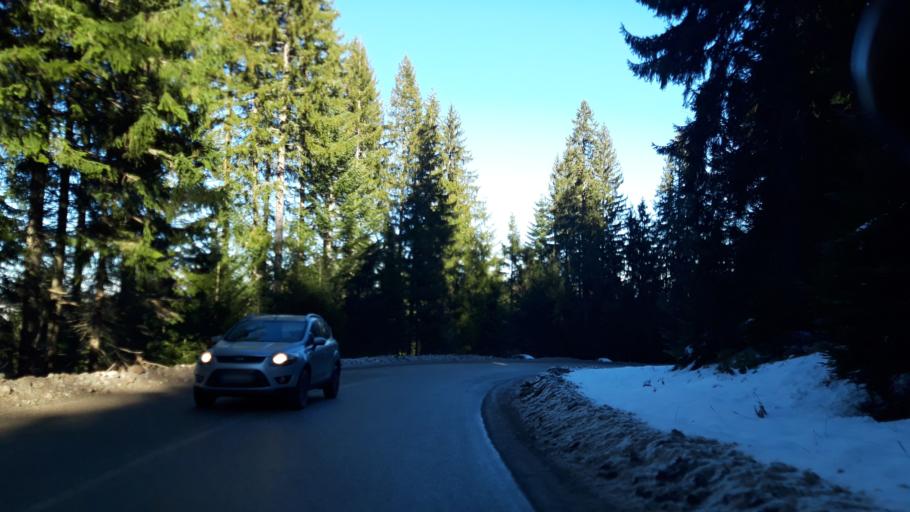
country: BA
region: Republika Srpska
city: Koran
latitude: 43.7787
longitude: 18.5527
